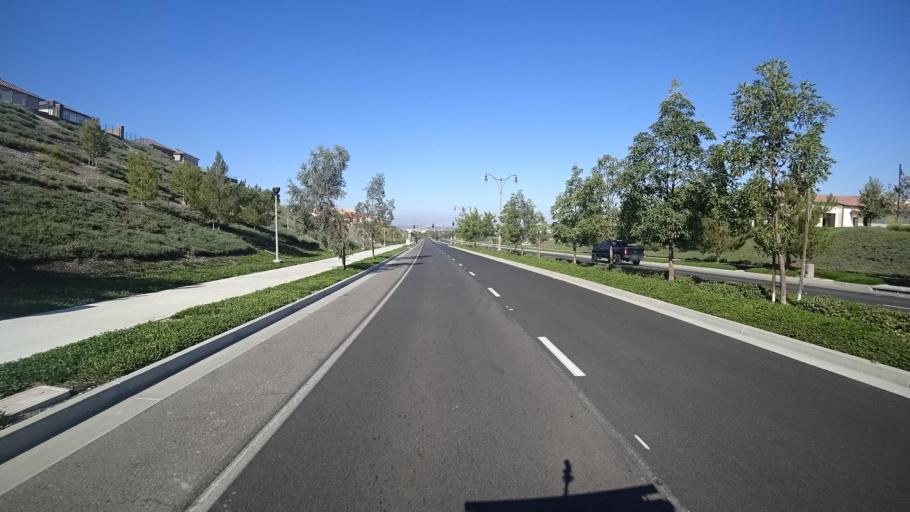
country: US
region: California
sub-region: Orange County
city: Foothill Ranch
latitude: 33.6948
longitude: -117.6997
